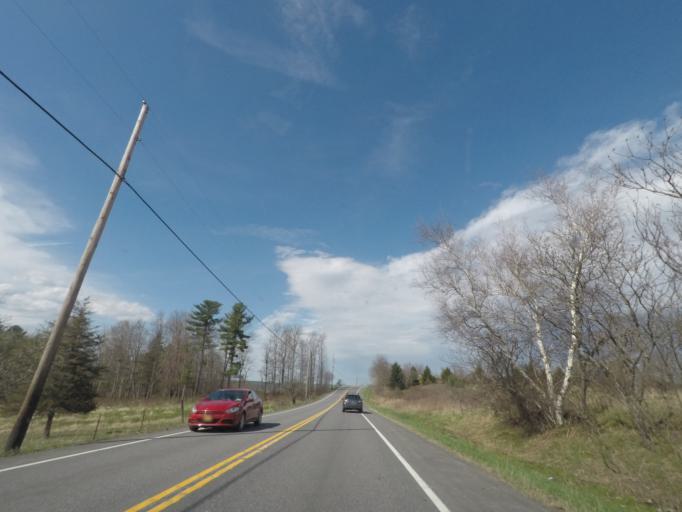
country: US
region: New York
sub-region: Greene County
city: Cairo
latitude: 42.4651
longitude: -74.0031
